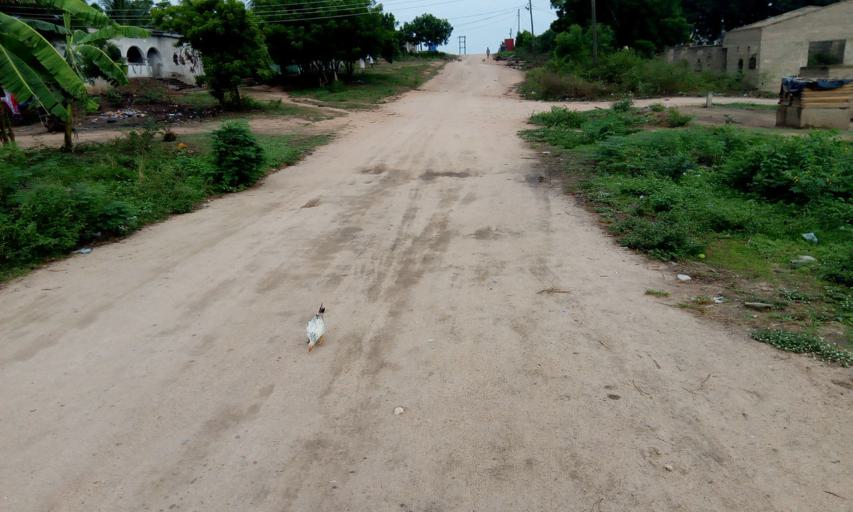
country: GH
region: Central
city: Winneba
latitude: 5.3563
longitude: -0.6172
